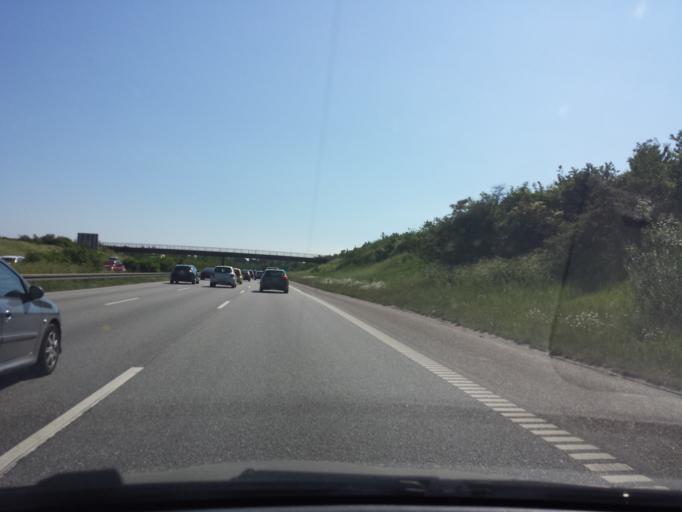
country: DK
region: Capital Region
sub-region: Frederiksberg Kommune
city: Frederiksberg
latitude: 55.6220
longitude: 12.5300
